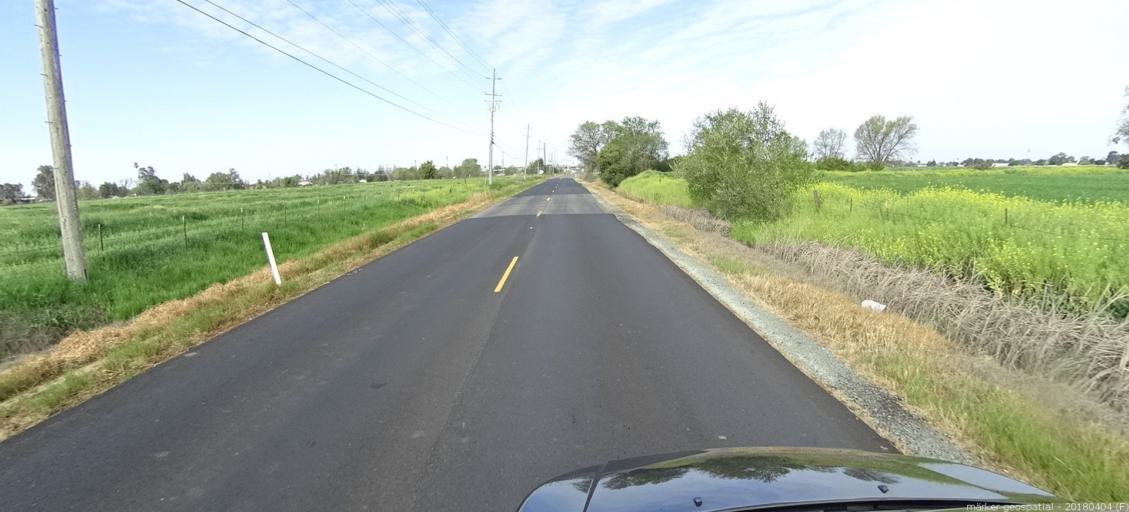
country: US
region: California
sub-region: Sacramento County
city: Galt
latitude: 38.2550
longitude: -121.2862
